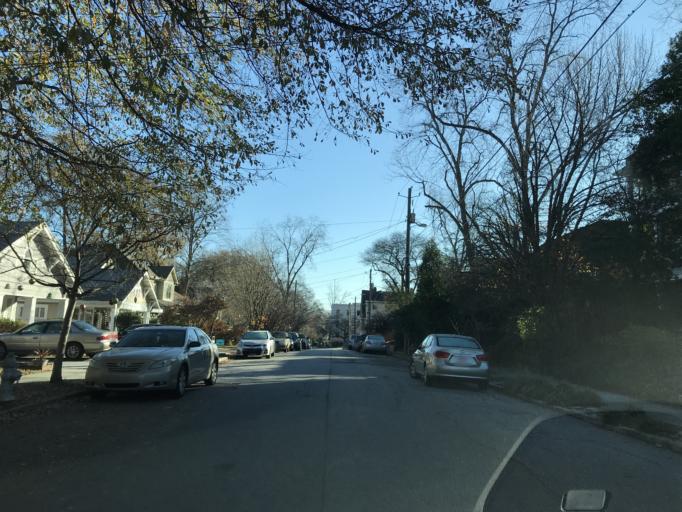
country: US
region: Georgia
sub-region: Fulton County
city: Atlanta
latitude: 33.7745
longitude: -84.3745
